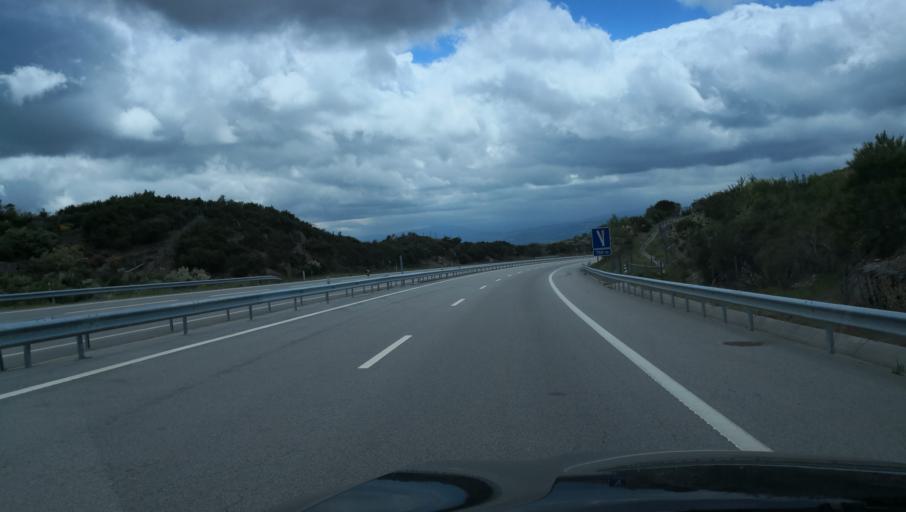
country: PT
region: Vila Real
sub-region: Vila Real
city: Vila Real
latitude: 41.3757
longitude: -7.6692
